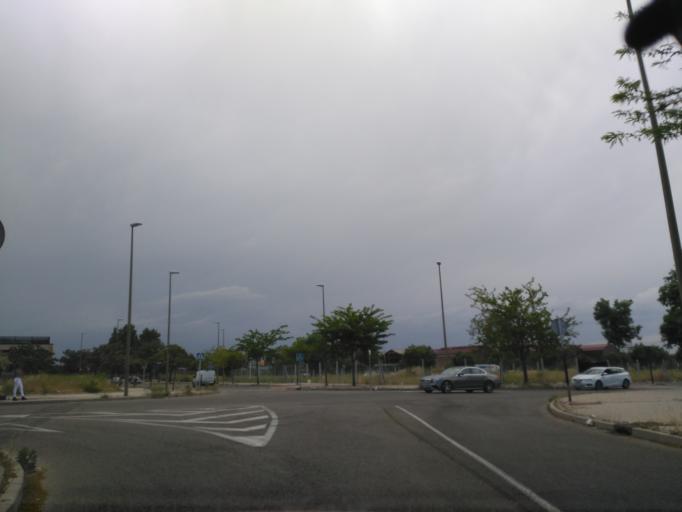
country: ES
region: Madrid
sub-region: Provincia de Madrid
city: Villaverde
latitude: 40.3366
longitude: -3.7176
